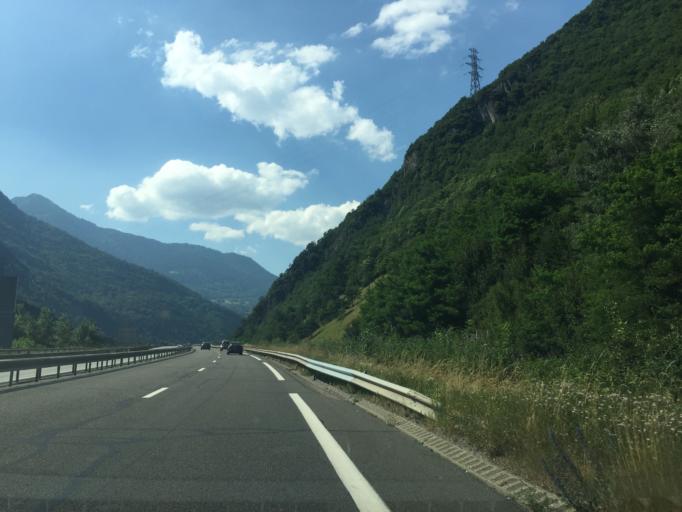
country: FR
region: Rhone-Alpes
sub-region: Departement de la Savoie
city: Aigueblanche
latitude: 45.5278
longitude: 6.4803
